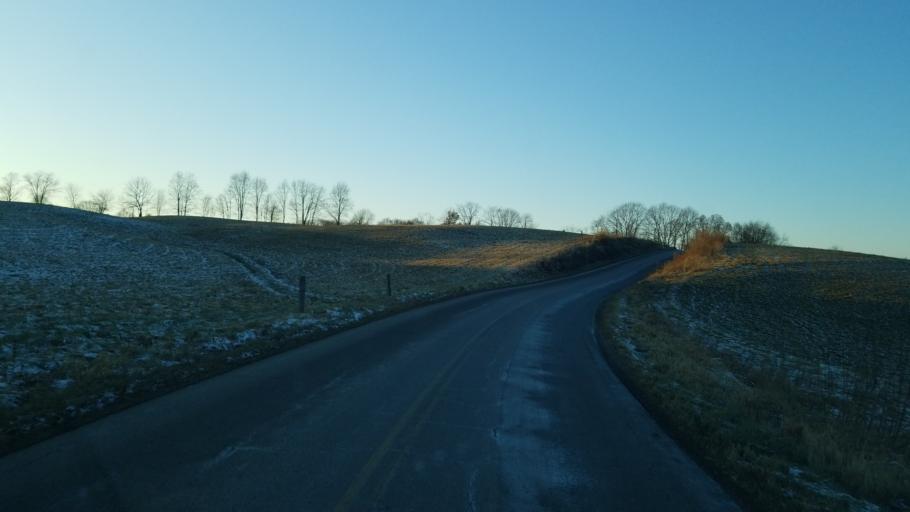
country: US
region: Ohio
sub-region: Wayne County
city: Shreve
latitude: 40.6629
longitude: -81.9682
